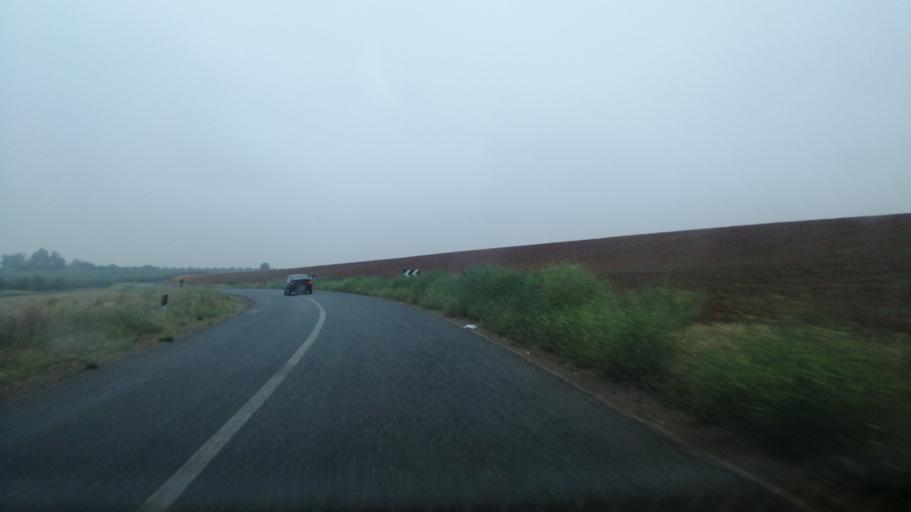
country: MA
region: Rabat-Sale-Zemmour-Zaer
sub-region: Khemisset
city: Tiflet
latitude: 33.7544
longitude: -6.2674
